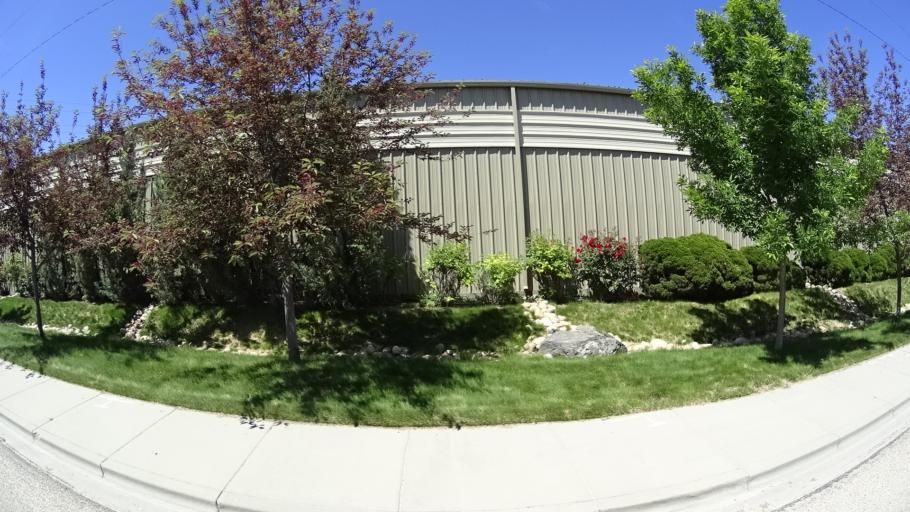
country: US
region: Idaho
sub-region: Ada County
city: Boise
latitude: 43.5639
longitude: -116.1835
